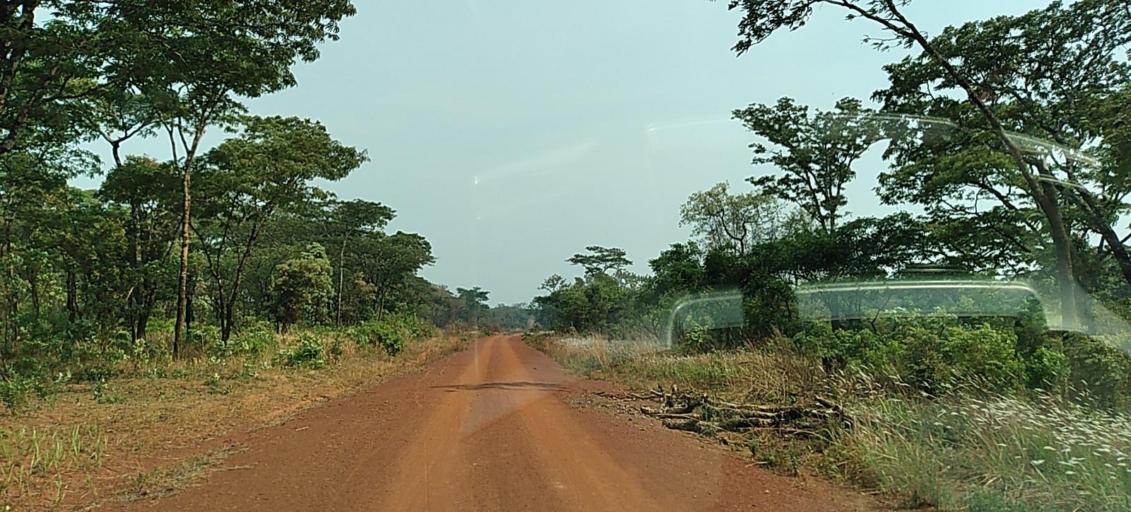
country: ZM
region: North-Western
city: Kansanshi
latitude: -12.0219
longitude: 26.8501
